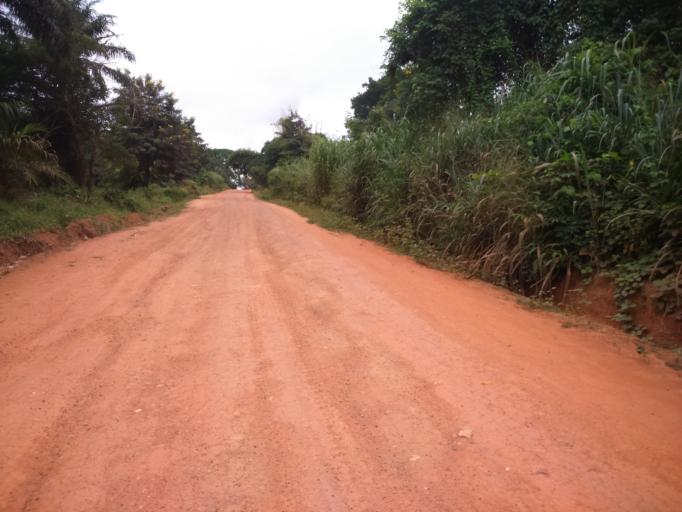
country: CI
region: Lagunes
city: Agou
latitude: 6.0873
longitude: -4.0661
